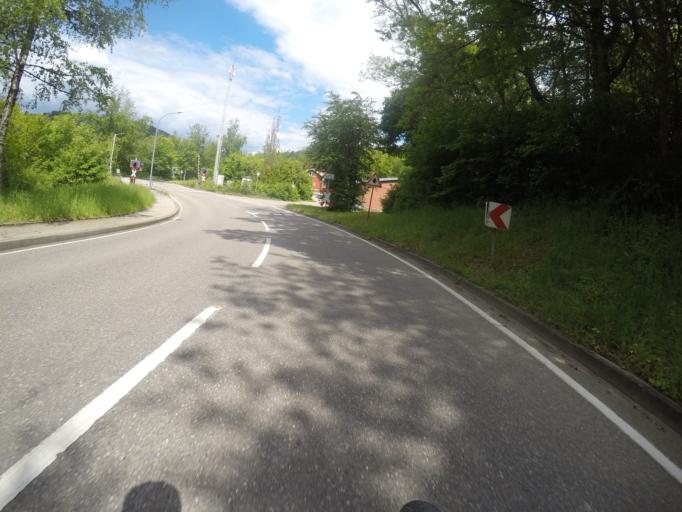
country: DE
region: Baden-Wuerttemberg
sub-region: Karlsruhe Region
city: Nagold
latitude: 48.5866
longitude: 8.7336
